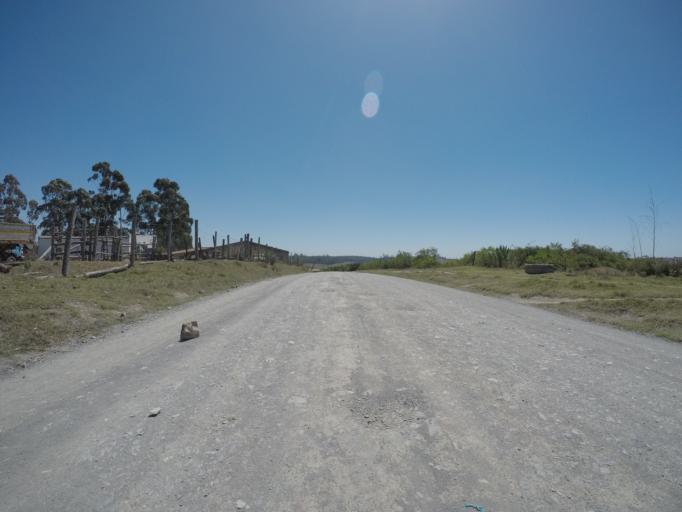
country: ZA
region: Eastern Cape
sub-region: OR Tambo District Municipality
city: Libode
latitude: -31.9732
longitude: 29.0315
